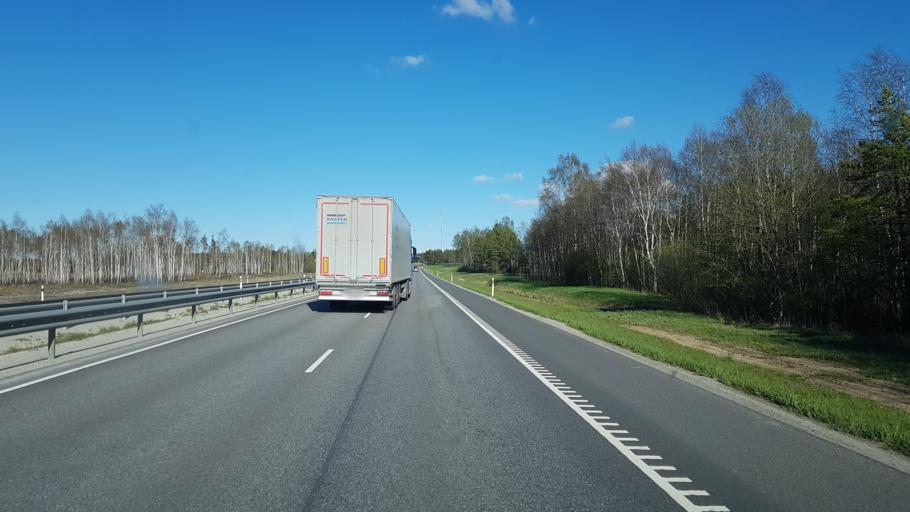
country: EE
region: Harju
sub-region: Saue vald
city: Laagri
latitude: 59.3127
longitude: 24.5948
